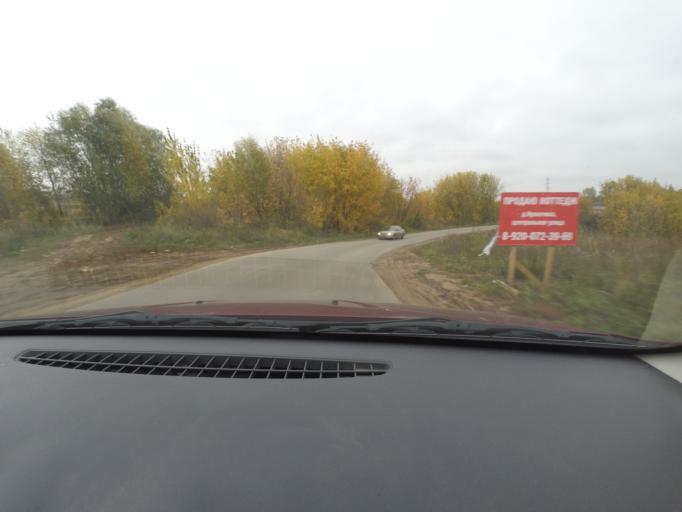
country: RU
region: Nizjnij Novgorod
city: Afonino
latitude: 56.2781
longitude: 44.0518
